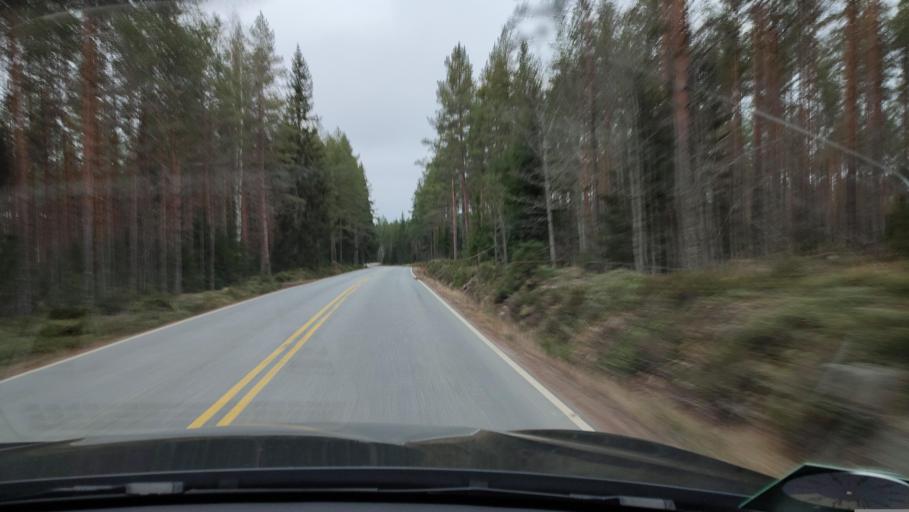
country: FI
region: Southern Ostrobothnia
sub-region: Suupohja
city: Karijoki
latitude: 62.2474
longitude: 21.7537
